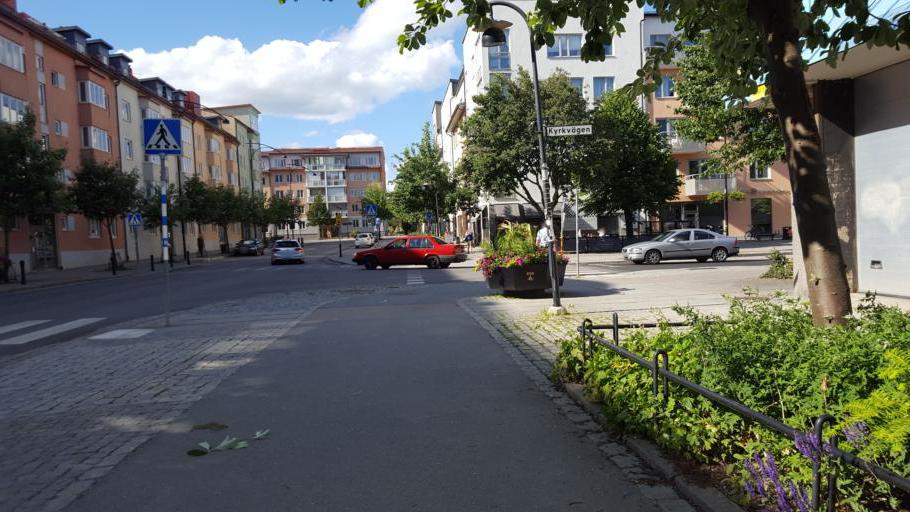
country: SE
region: Stockholm
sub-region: Upplands Vasby Kommun
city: Upplands Vaesby
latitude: 59.5196
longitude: 17.9095
